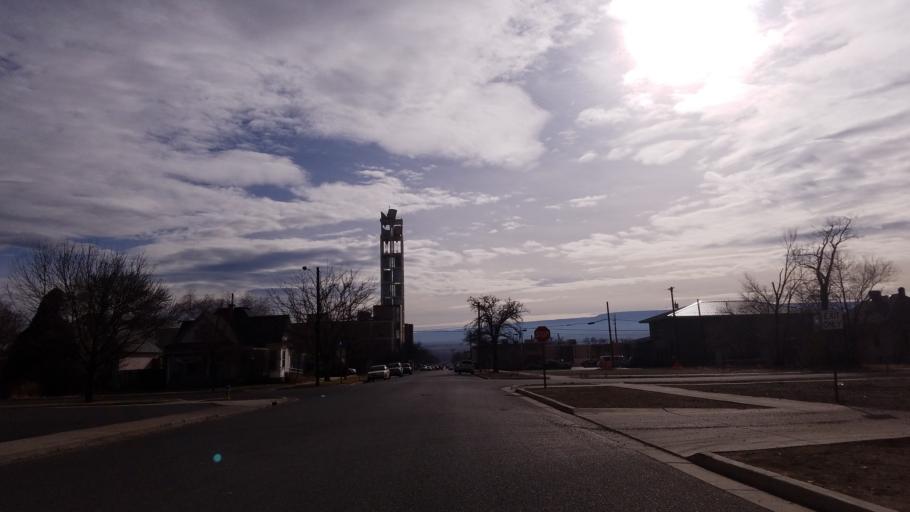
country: US
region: Colorado
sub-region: Mesa County
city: Grand Junction
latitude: 39.0697
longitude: -108.5594
